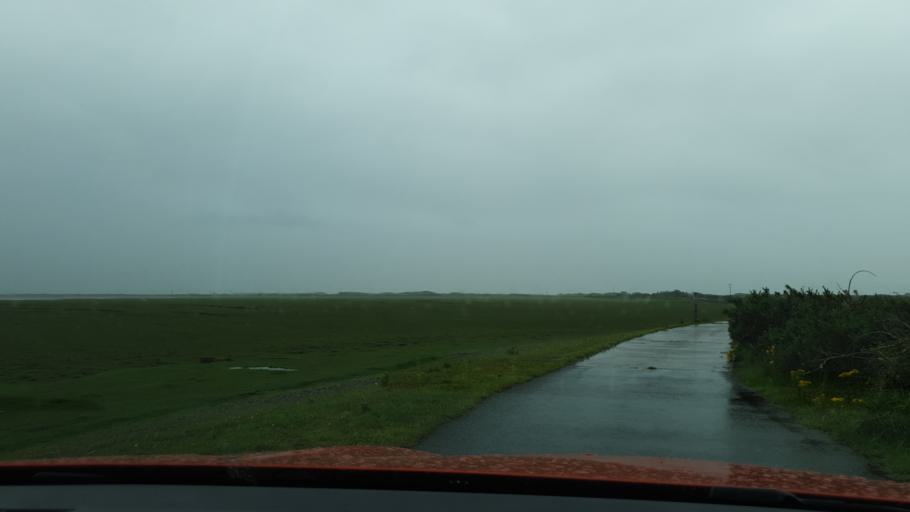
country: GB
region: England
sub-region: Cumbria
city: Barrow in Furness
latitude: 54.0541
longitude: -3.2075
